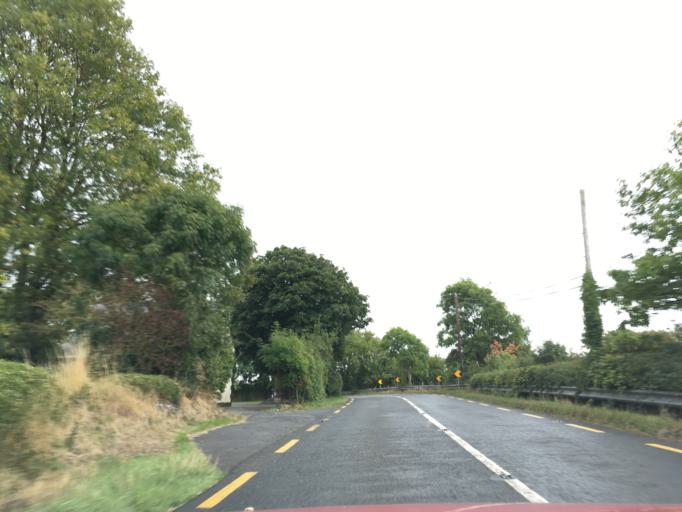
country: IE
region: Munster
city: Fethard
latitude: 52.4327
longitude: -7.7859
